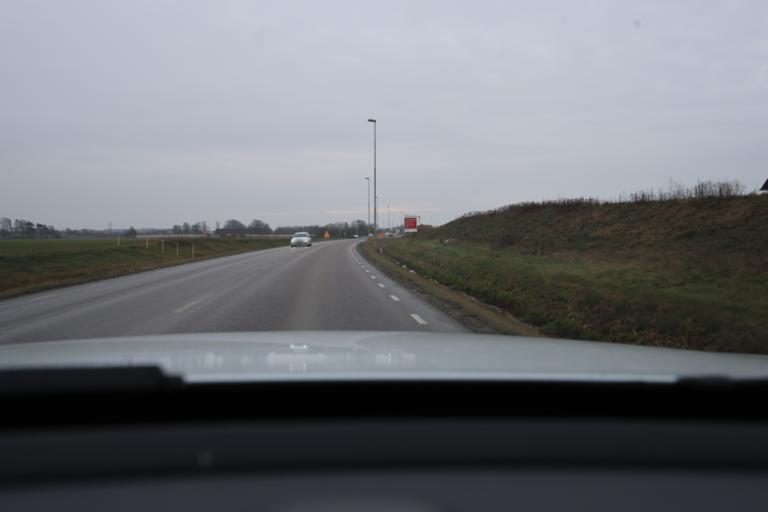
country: SE
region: Halland
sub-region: Varbergs Kommun
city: Traslovslage
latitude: 57.0920
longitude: 12.2932
